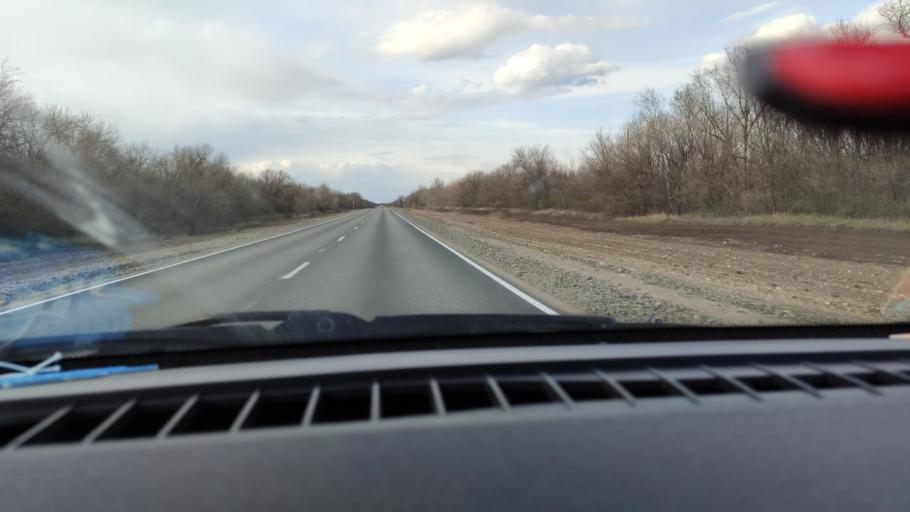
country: RU
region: Saratov
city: Privolzhskiy
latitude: 51.1442
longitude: 45.9613
